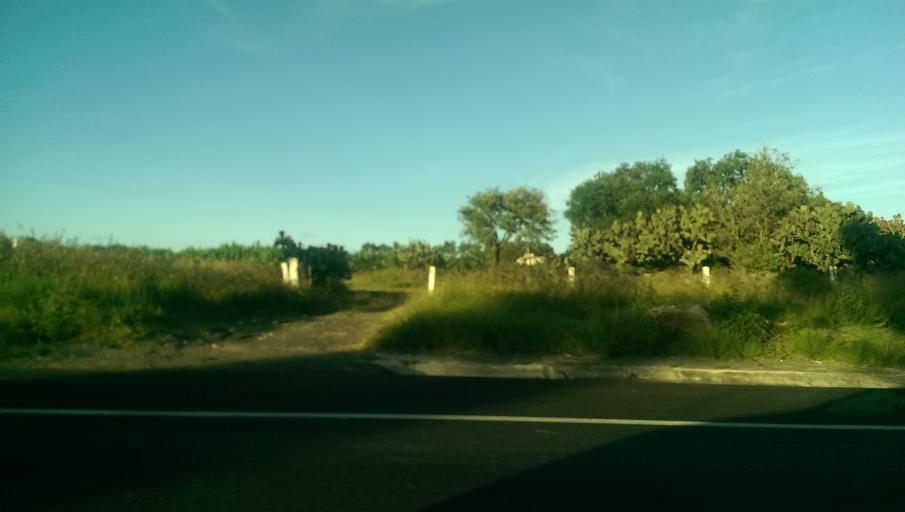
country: MX
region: Mexico
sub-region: Aculco
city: El Colorado
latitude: 20.1915
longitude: -99.7745
